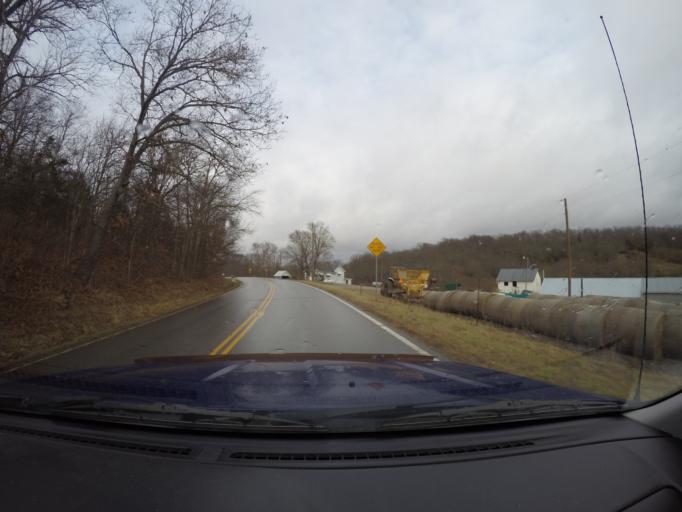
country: US
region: Kansas
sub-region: Leavenworth County
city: Leavenworth
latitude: 39.3377
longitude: -95.1339
